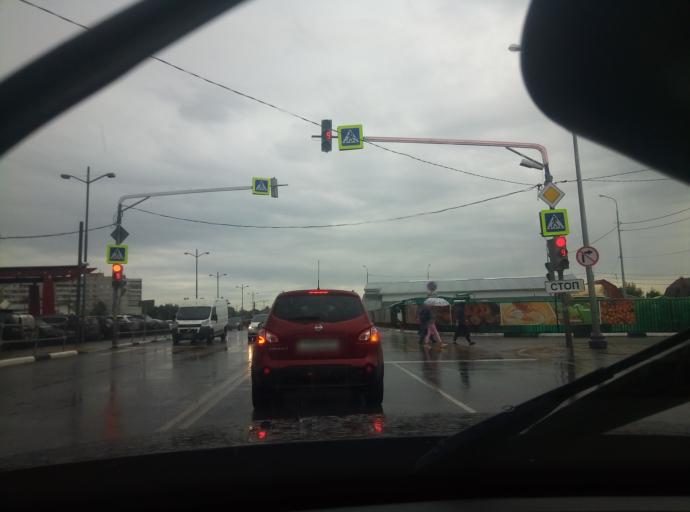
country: RU
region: Moskovskaya
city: Serpukhov
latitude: 54.9172
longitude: 37.4246
